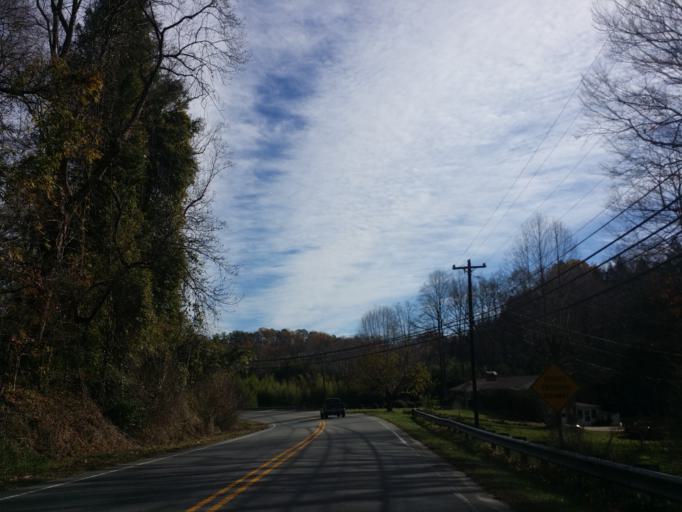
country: US
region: North Carolina
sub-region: McDowell County
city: West Marion
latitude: 35.6843
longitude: -82.0848
